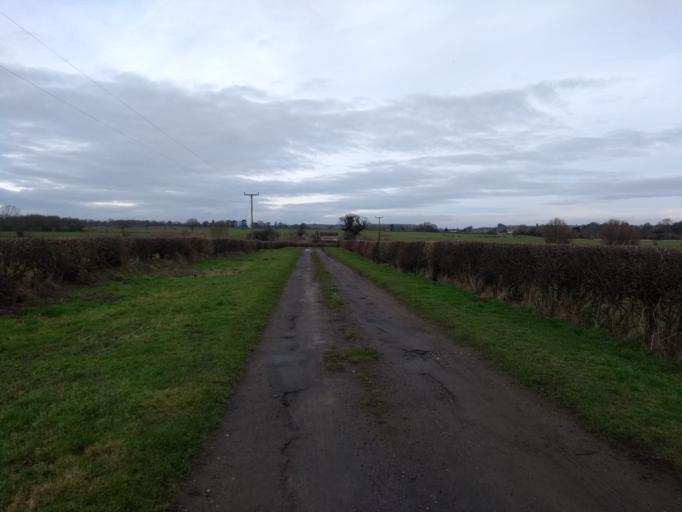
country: GB
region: England
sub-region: East Riding of Yorkshire
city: Stamford Bridge
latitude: 54.0669
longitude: -0.9326
